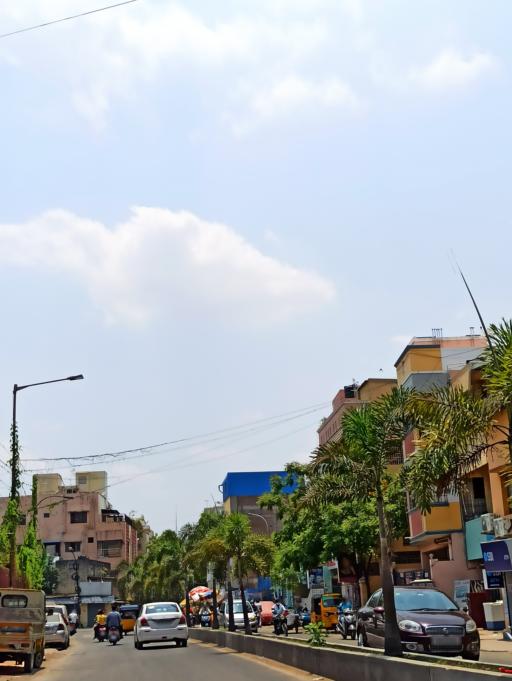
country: IN
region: Tamil Nadu
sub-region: Chennai
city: Chetput
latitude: 13.0929
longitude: 80.2328
